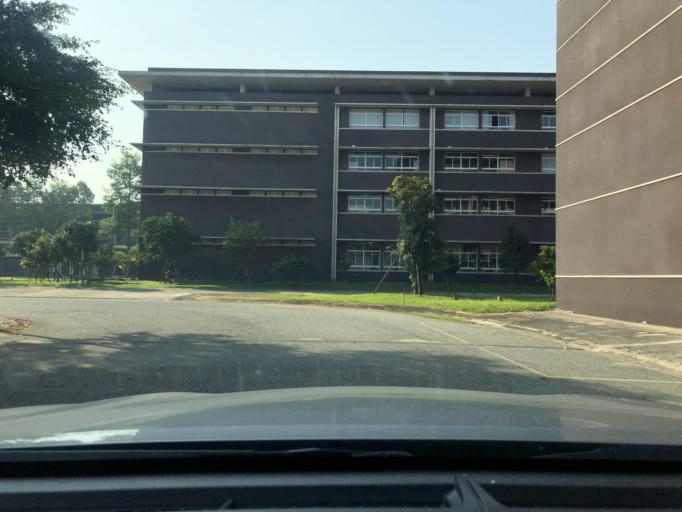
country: VN
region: Binh Duong
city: Thu Dau Mot
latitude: 11.0549
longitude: 106.6669
